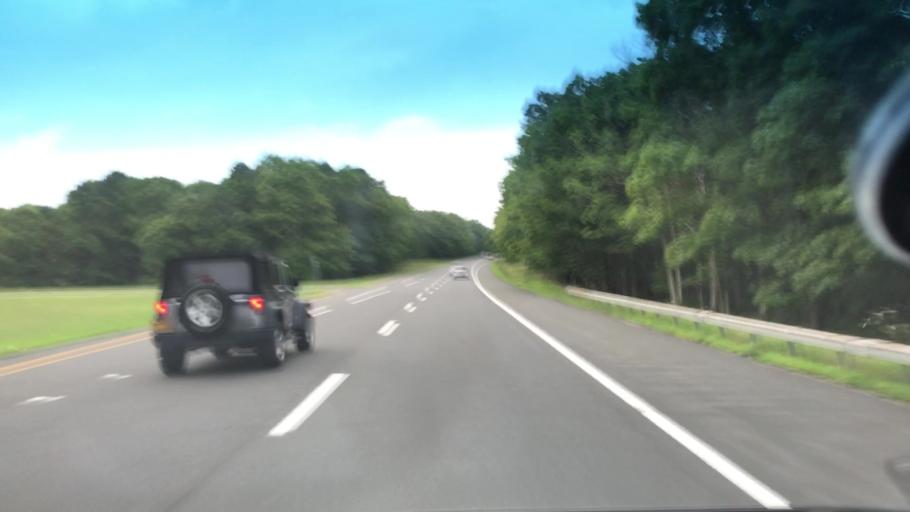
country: US
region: New York
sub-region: Suffolk County
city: East Shoreham
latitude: 40.9200
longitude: -72.8797
